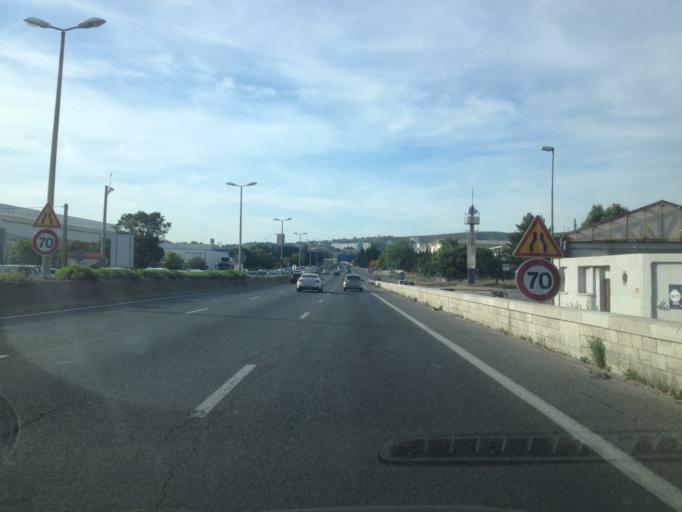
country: FR
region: Provence-Alpes-Cote d'Azur
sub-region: Departement des Bouches-du-Rhone
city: Marseille 14
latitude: 43.3323
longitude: 5.3777
